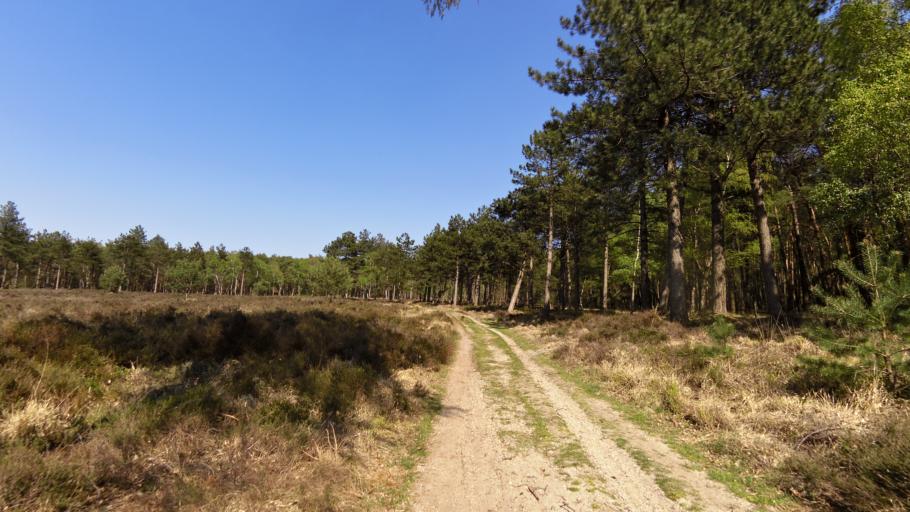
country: NL
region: Gelderland
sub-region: Gemeente Rozendaal
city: Rozendaal
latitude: 52.0378
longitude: 5.9565
